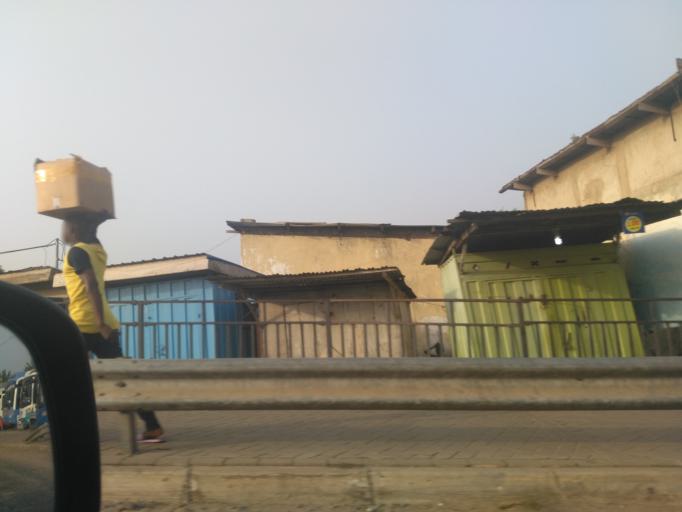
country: GH
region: Greater Accra
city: Dome
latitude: 5.6202
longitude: -0.2314
